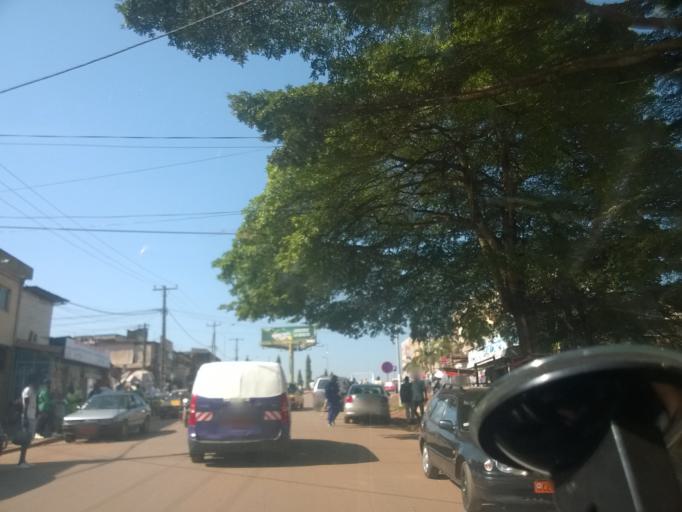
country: CM
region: Centre
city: Yaounde
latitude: 3.8369
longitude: 11.4849
